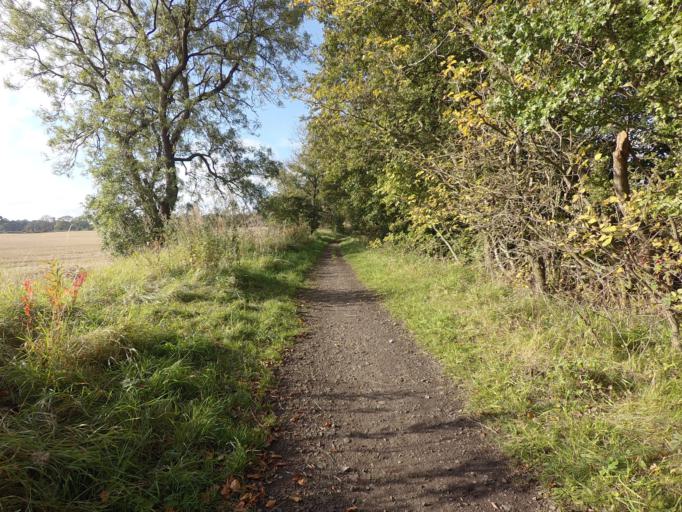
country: GB
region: Scotland
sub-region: West Lothian
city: East Calder
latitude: 55.9042
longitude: -3.4691
